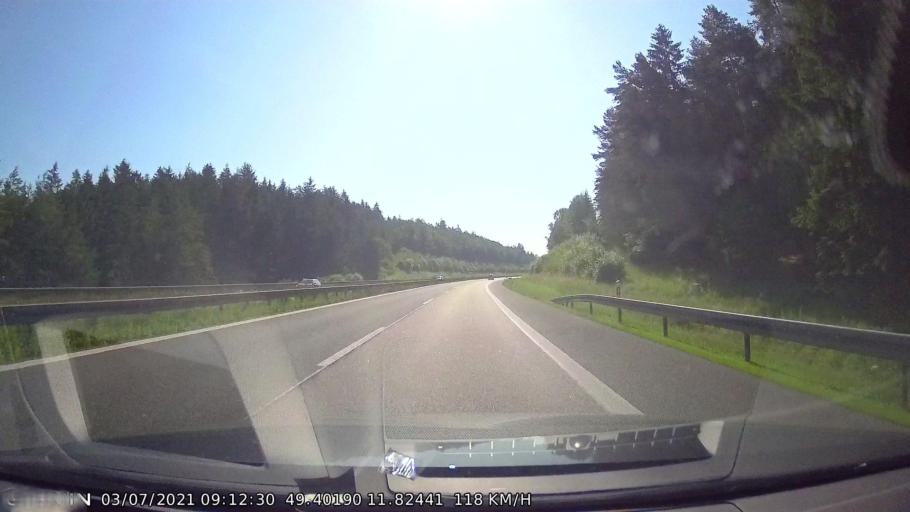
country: DE
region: Bavaria
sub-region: Upper Palatinate
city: Amberg
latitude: 49.4019
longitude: 11.8249
